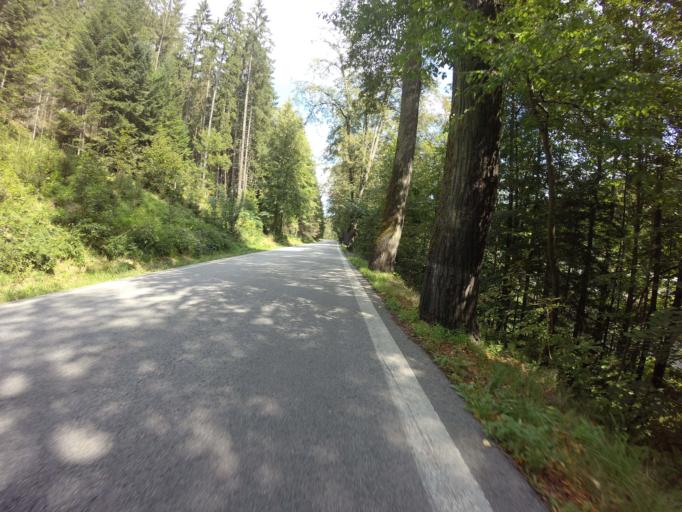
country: CZ
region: Jihocesky
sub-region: Okres Cesky Krumlov
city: Vyssi Brod
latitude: 48.6591
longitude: 14.3638
